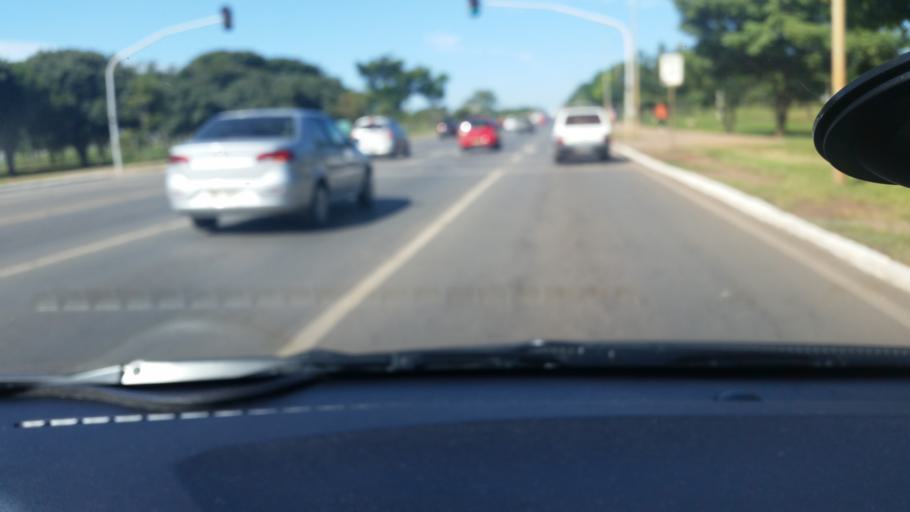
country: BR
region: Federal District
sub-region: Brasilia
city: Brasilia
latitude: -15.7789
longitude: -47.9337
